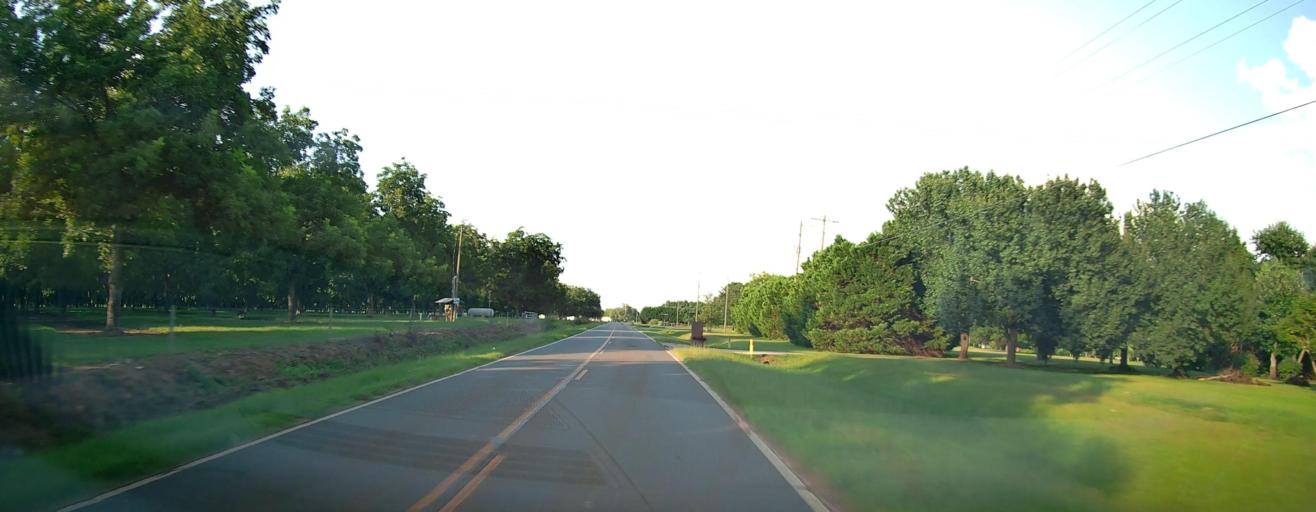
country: US
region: Georgia
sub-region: Peach County
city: Byron
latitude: 32.6300
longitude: -83.8133
